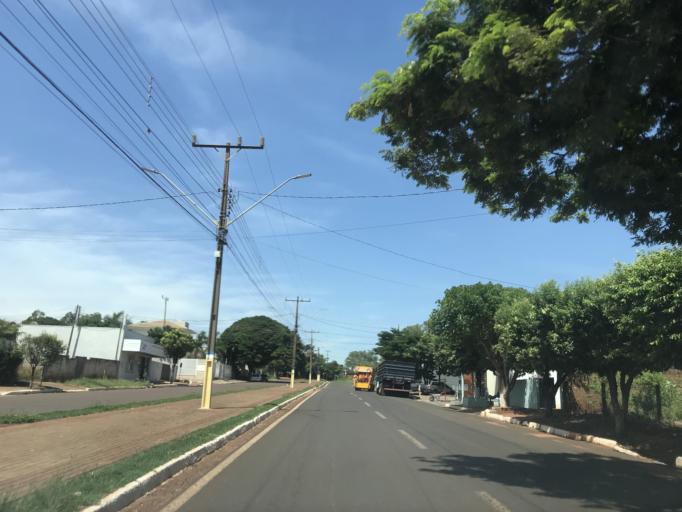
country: BR
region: Parana
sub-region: Paranavai
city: Nova Aurora
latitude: -22.9430
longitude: -52.6919
